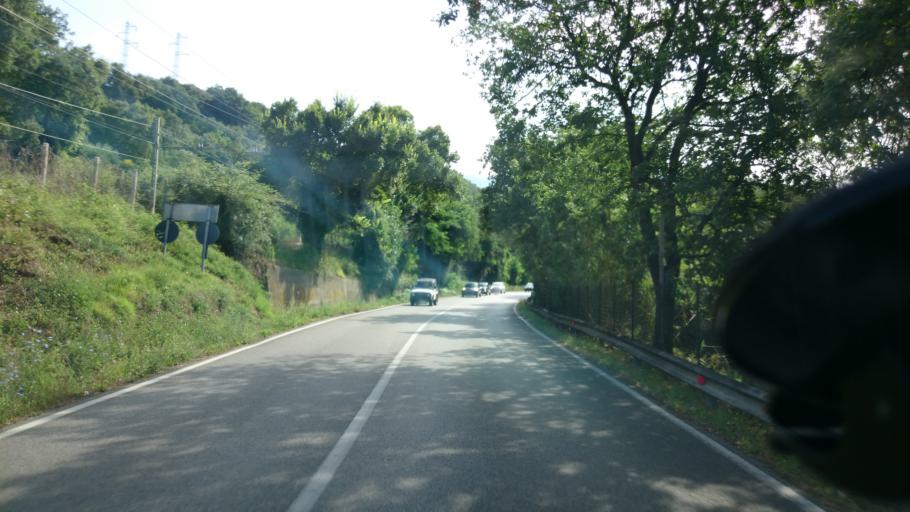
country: IT
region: Campania
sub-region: Provincia di Salerno
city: Ispani
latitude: 40.0798
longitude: 15.5742
